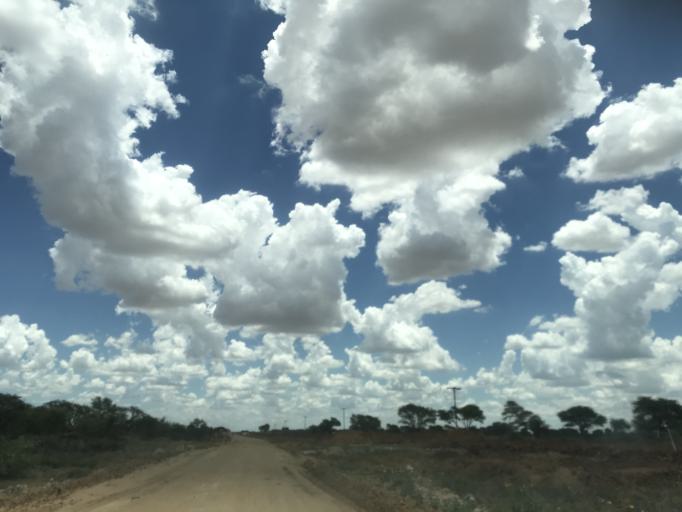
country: BW
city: Mabuli
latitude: -25.7905
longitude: 24.6489
